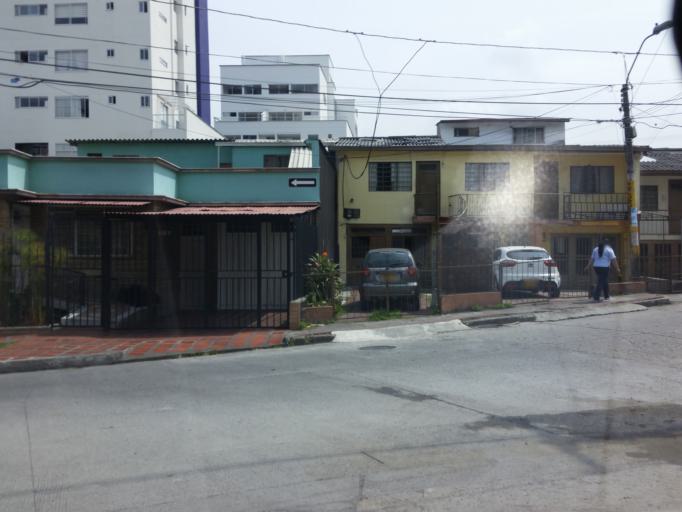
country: CO
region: Caldas
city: Manizales
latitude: 5.0748
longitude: -75.5258
